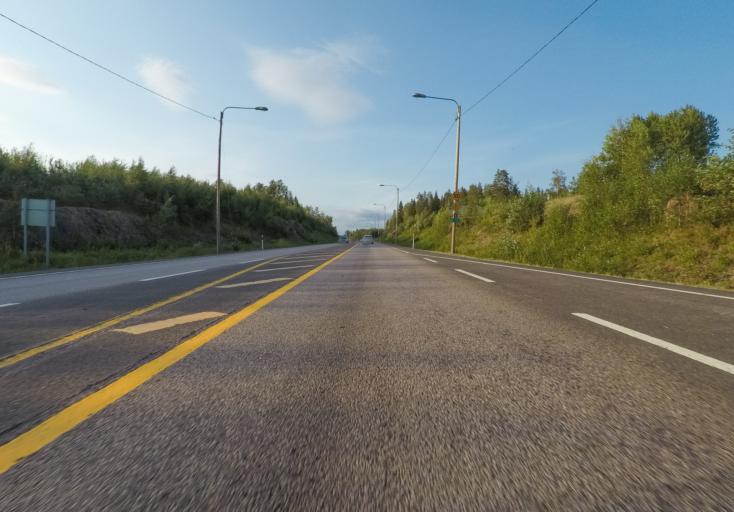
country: FI
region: Paijanne Tavastia
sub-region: Lahti
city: Heinola
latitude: 61.3477
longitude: 26.0442
